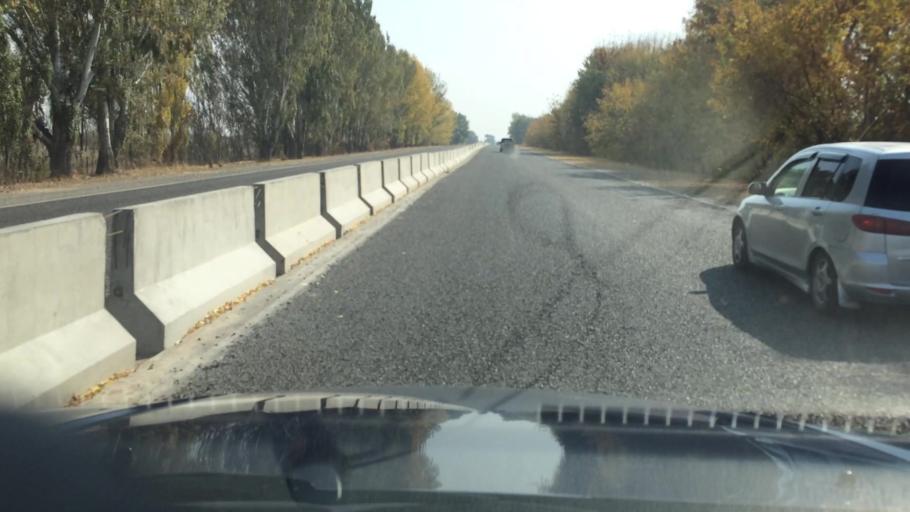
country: KG
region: Chuy
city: Kant
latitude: 42.9642
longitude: 74.9147
